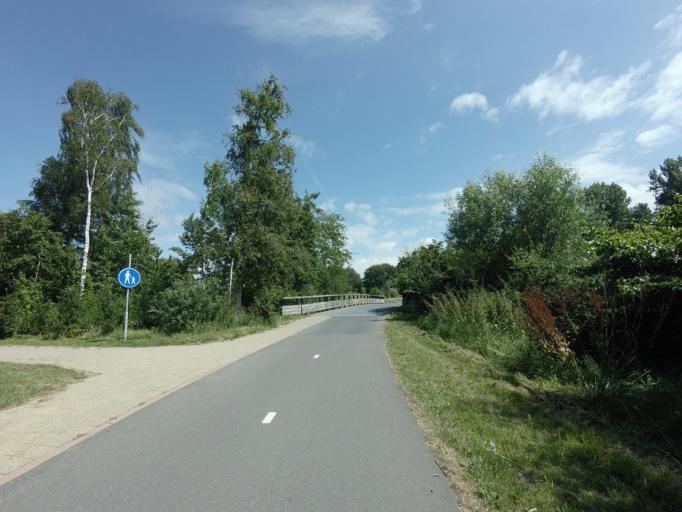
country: NL
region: Flevoland
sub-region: Gemeente Almere
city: Almere Stad
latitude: 52.3413
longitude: 5.2116
